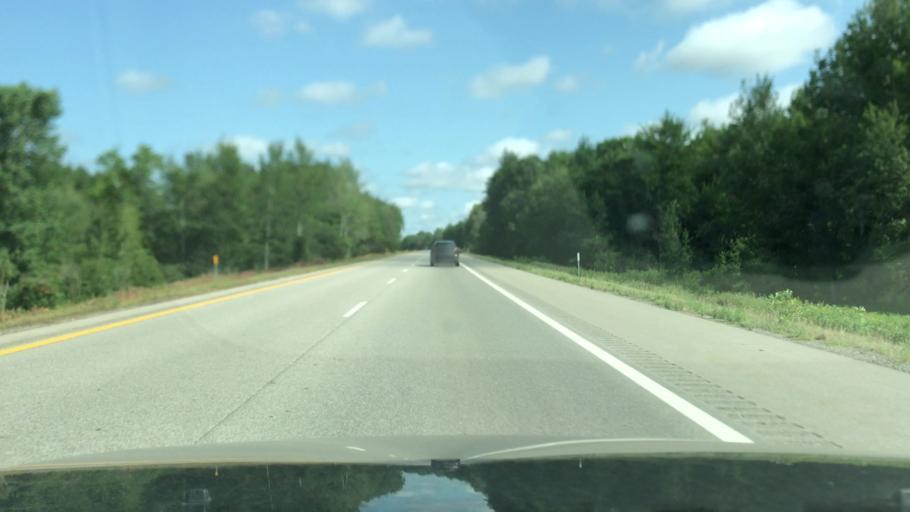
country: US
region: Michigan
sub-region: Montcalm County
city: Howard City
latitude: 43.5422
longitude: -85.4861
